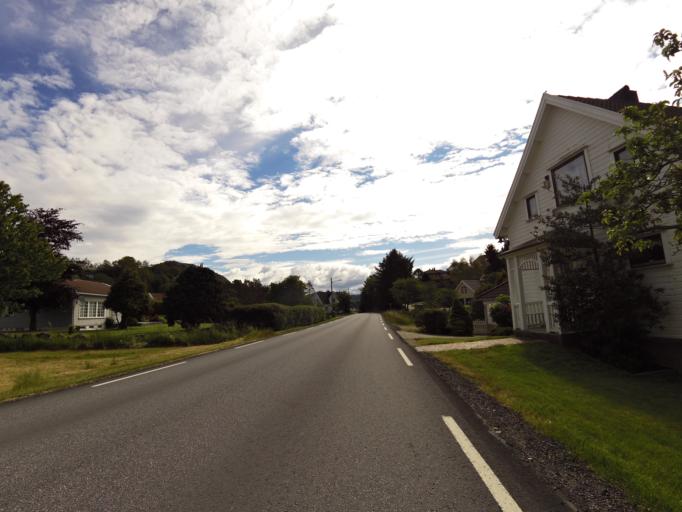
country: NO
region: Vest-Agder
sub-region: Lyngdal
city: Lyngdal
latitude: 58.0459
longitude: 7.1564
